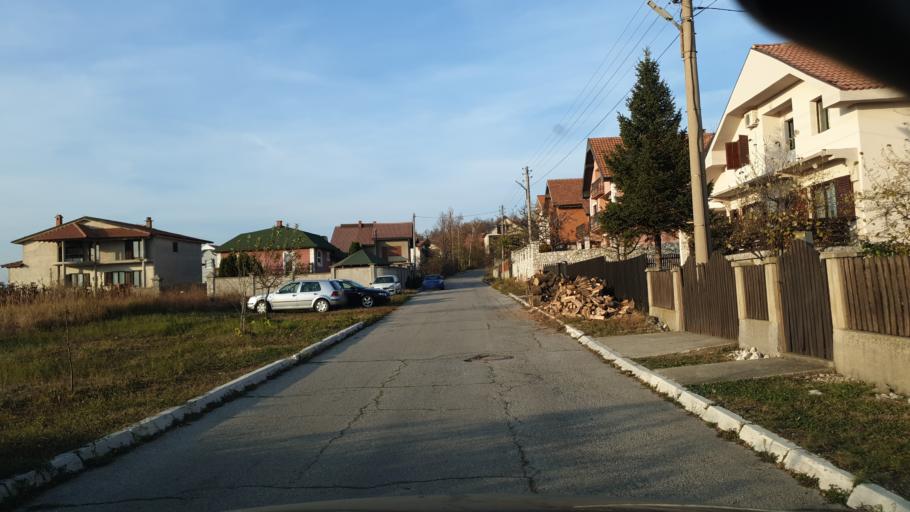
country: RS
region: Central Serbia
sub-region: Borski Okrug
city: Bor
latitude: 44.0564
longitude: 22.0816
